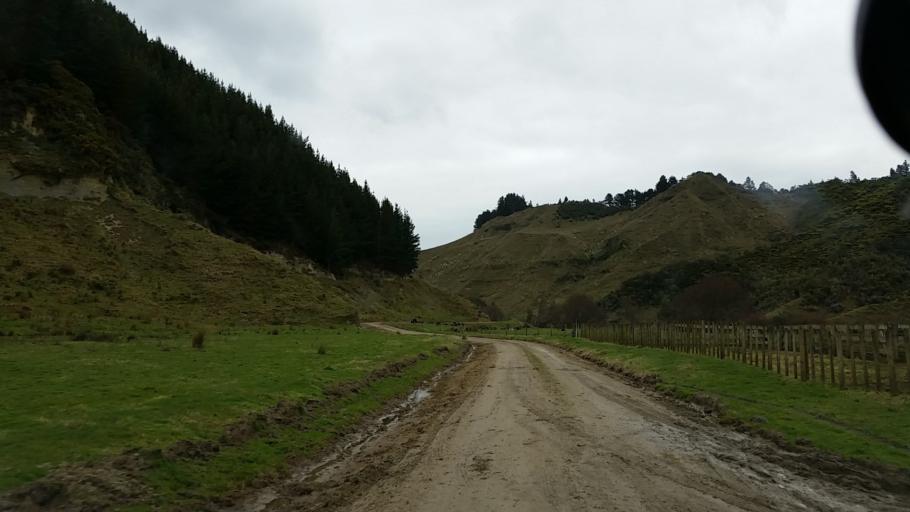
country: NZ
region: Taranaki
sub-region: South Taranaki District
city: Patea
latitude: -39.6598
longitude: 174.7502
